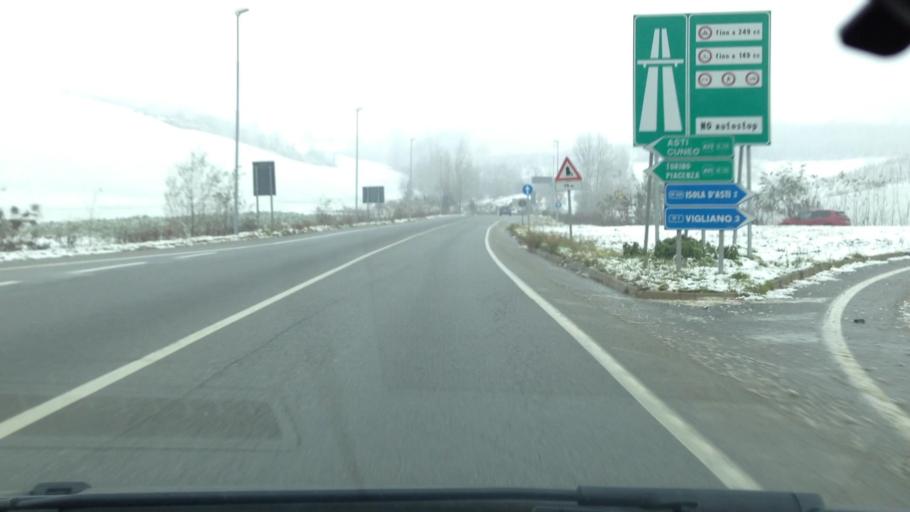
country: IT
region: Piedmont
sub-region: Provincia di Asti
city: Piano-Molini d'Isola
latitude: 44.8299
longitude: 8.2036
